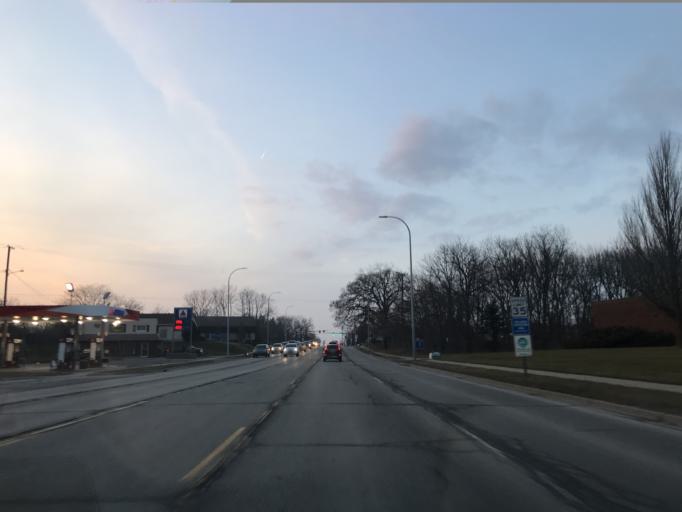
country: US
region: Michigan
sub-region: Livingston County
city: Brighton
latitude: 42.5232
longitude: -83.7691
